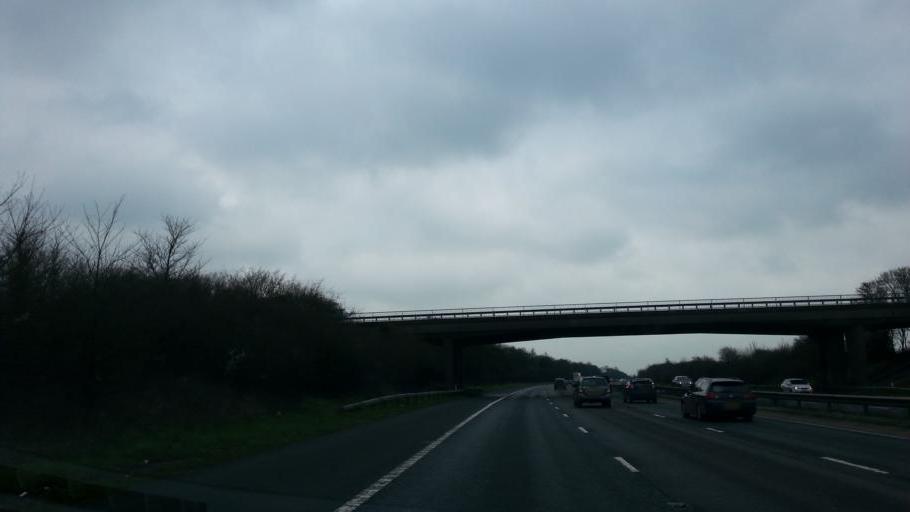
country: GB
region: England
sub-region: South Gloucestershire
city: Alveston
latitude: 51.5727
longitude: -2.5245
